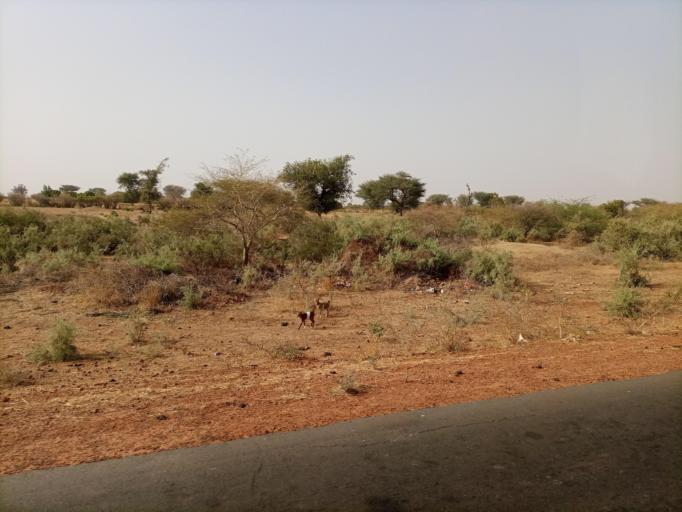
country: SN
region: Fatick
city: Foundiougne
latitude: 14.1237
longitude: -16.4256
